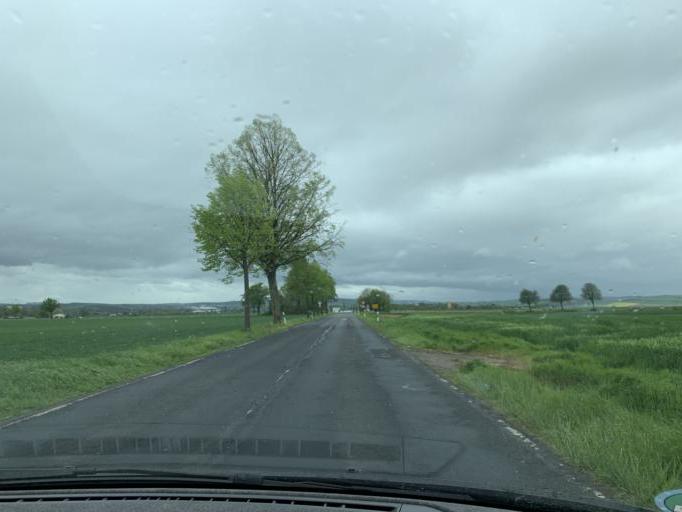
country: DE
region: North Rhine-Westphalia
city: Zulpich
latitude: 50.6796
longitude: 6.6427
